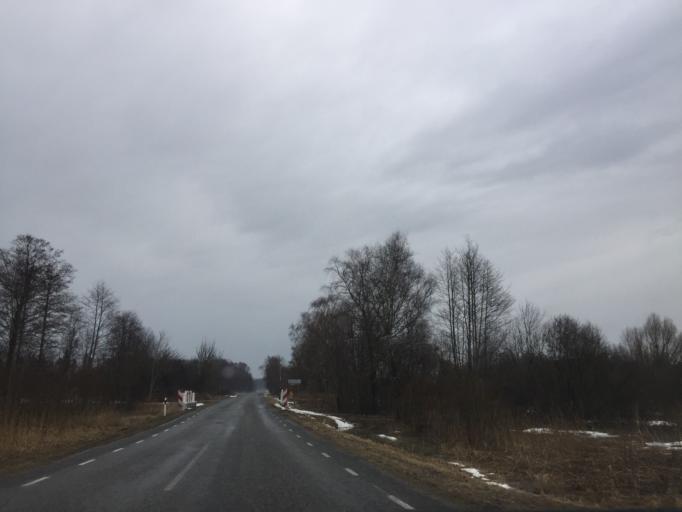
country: EE
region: Saare
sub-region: Orissaare vald
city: Orissaare
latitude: 58.5730
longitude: 23.0309
